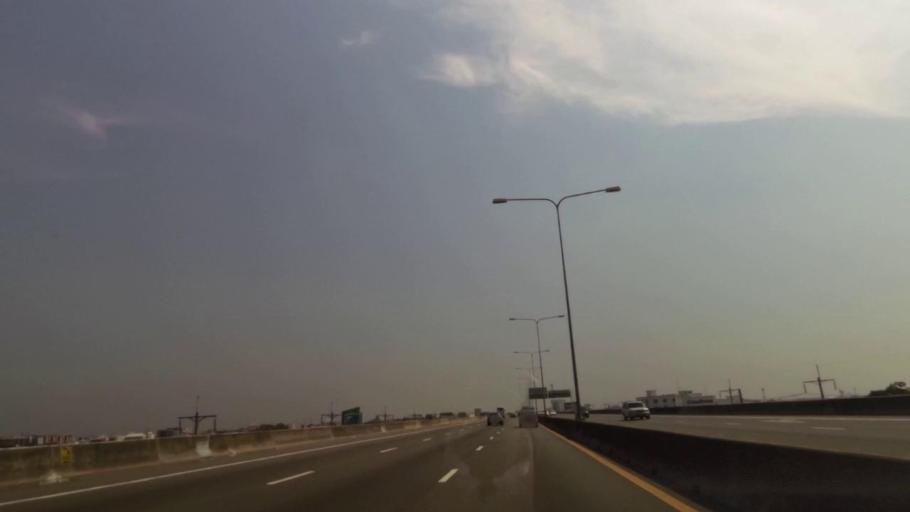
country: TH
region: Samut Prakan
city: Bang Bo District
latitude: 13.6180
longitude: 100.7452
